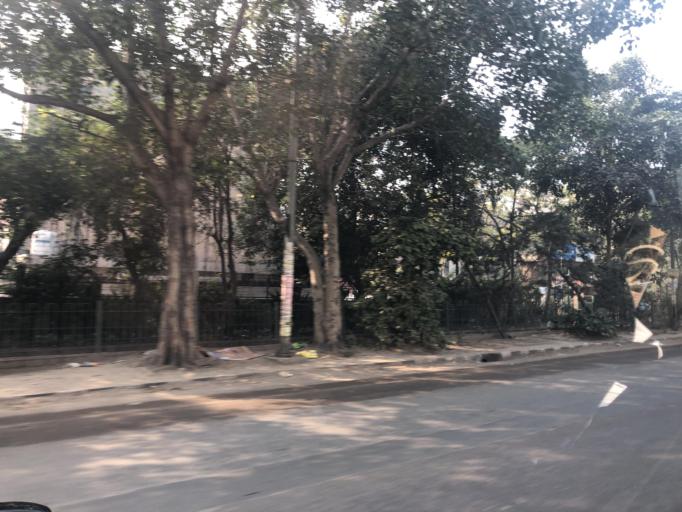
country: IN
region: NCT
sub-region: North West Delhi
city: Pitampura
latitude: 28.6758
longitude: 77.1238
